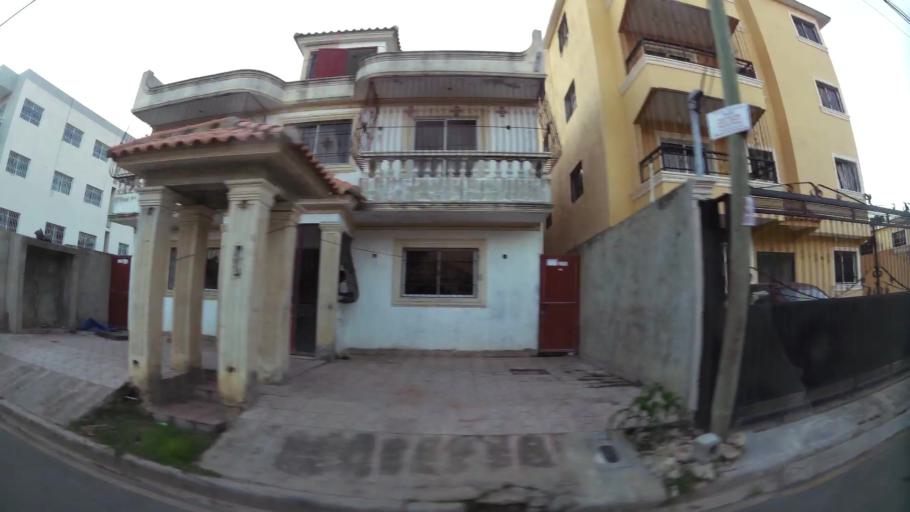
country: DO
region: Santo Domingo
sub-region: Santo Domingo
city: Santo Domingo Este
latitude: 18.4877
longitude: -69.8214
